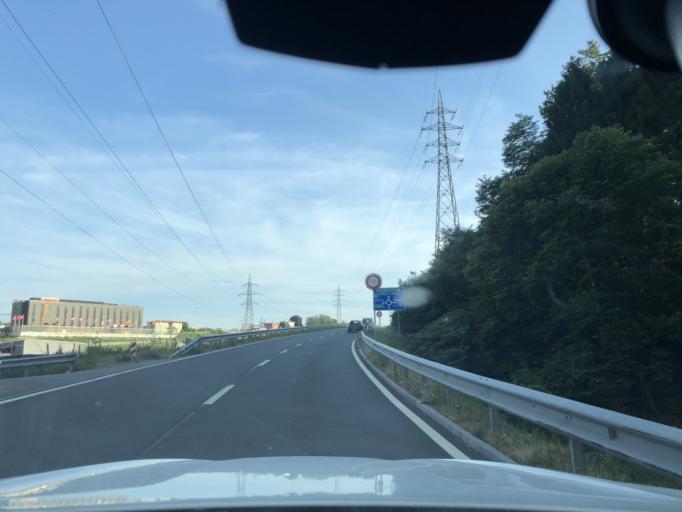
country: CH
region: Ticino
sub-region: Mendrisio District
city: Mendrisio
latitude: 45.8756
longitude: 8.9751
